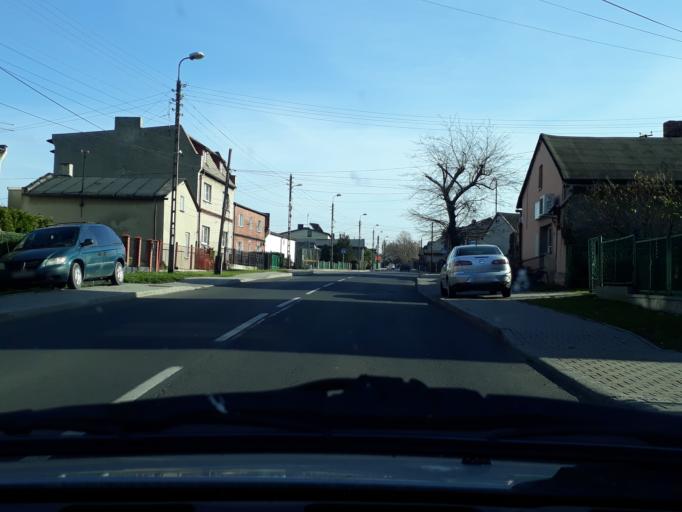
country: PL
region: Silesian Voivodeship
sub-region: Powiat tarnogorski
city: Tarnowskie Gory
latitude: 50.4214
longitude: 18.8762
